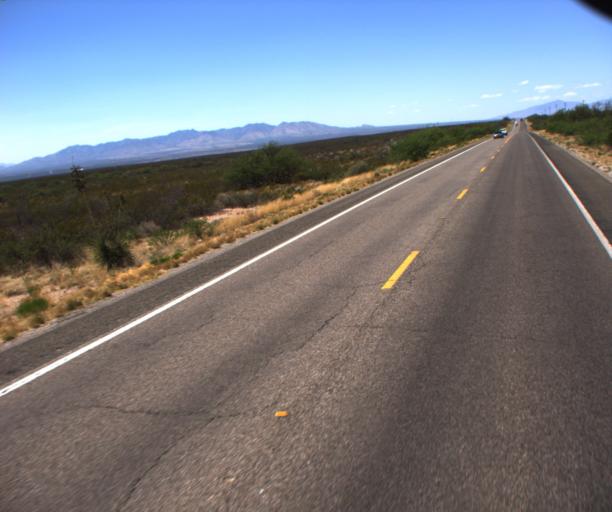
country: US
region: Arizona
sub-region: Cochise County
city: Tombstone
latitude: 31.7628
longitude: -110.1146
